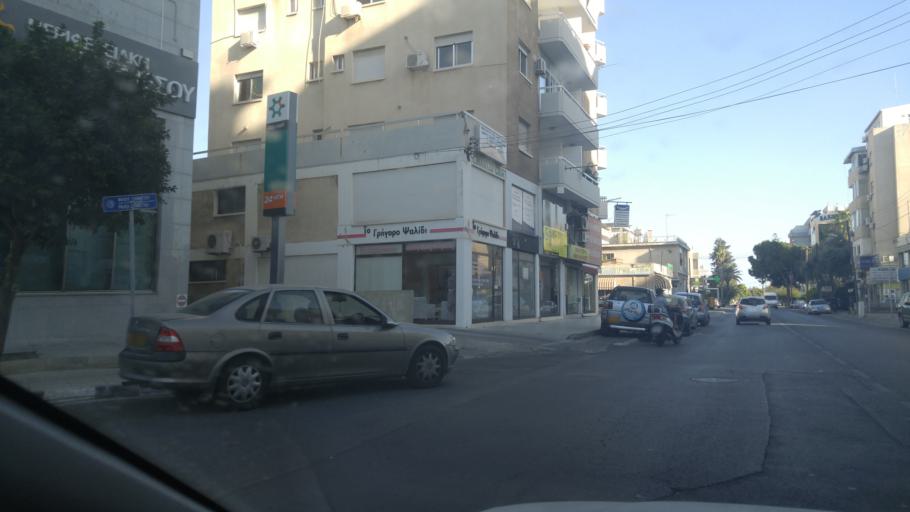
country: CY
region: Limassol
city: Limassol
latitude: 34.6812
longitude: 33.0339
